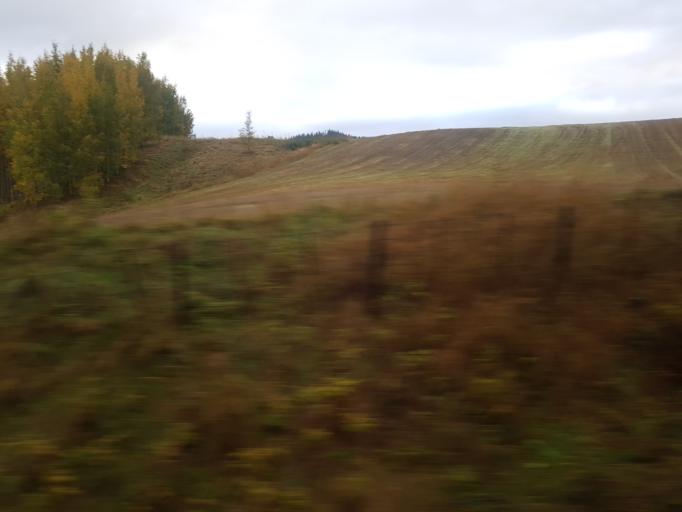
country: NO
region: Sor-Trondelag
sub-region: Melhus
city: Lundamo
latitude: 63.1925
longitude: 10.3074
